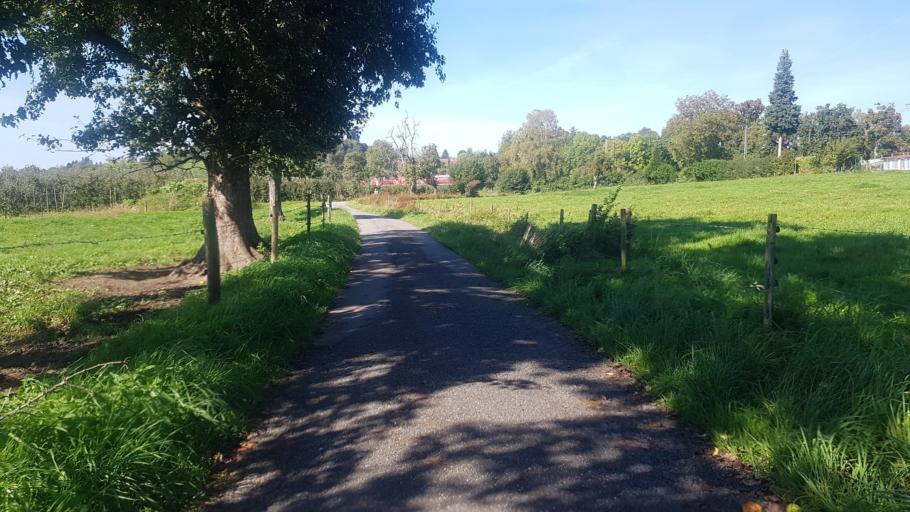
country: DE
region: Bavaria
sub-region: Swabia
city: Lindau
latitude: 47.5605
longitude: 9.6829
